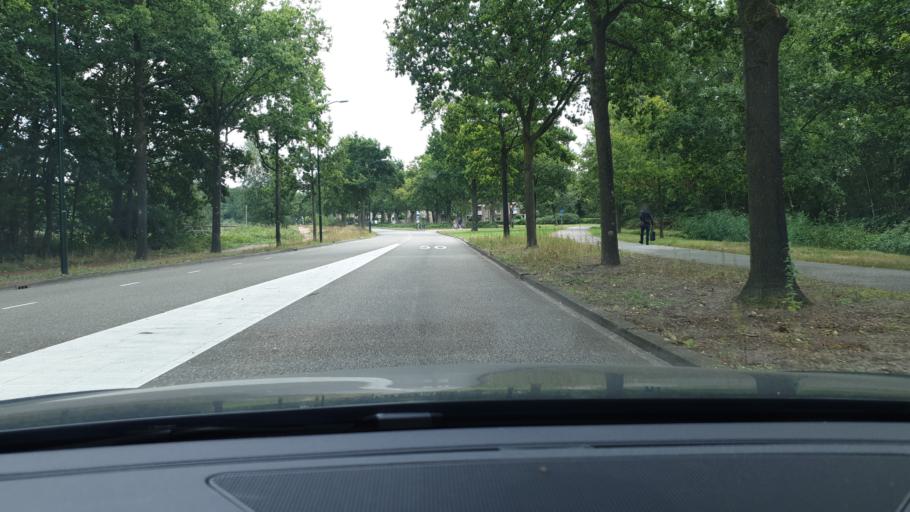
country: NL
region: North Brabant
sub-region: Gemeente Waalre
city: Waalre
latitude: 51.4017
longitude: 5.4806
